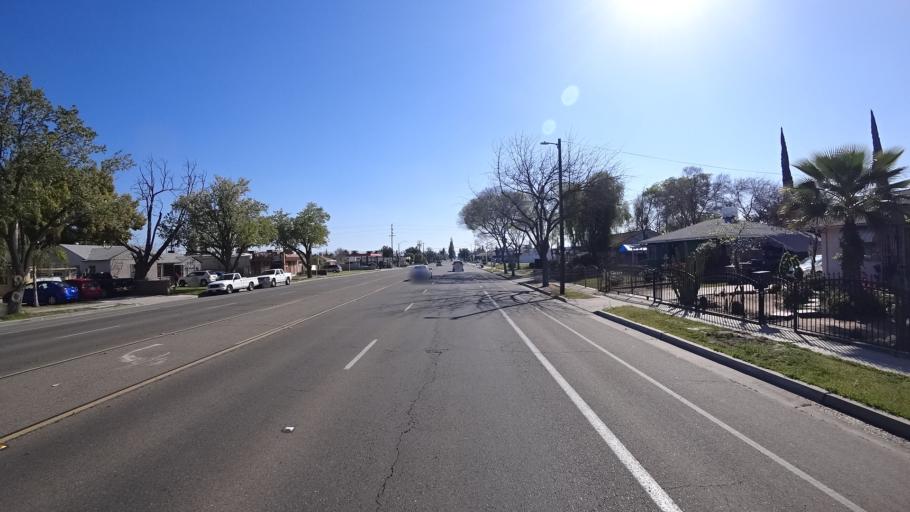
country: US
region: California
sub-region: Fresno County
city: Fresno
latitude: 36.7793
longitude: -119.8191
